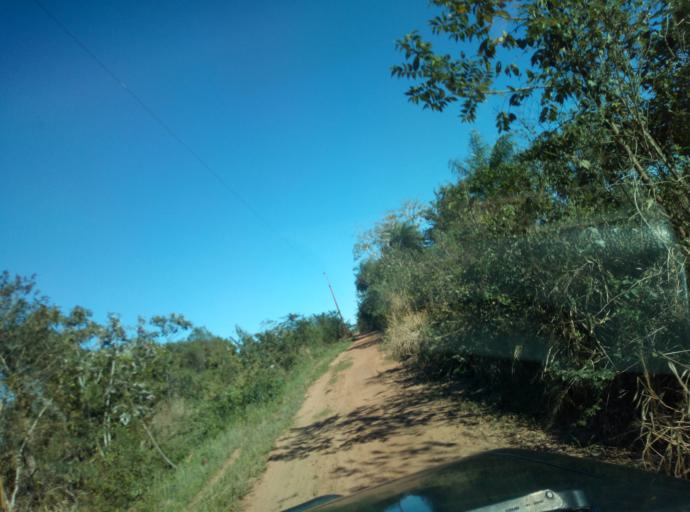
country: PY
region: Caaguazu
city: Doctor Cecilio Baez
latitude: -25.1790
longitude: -56.2347
